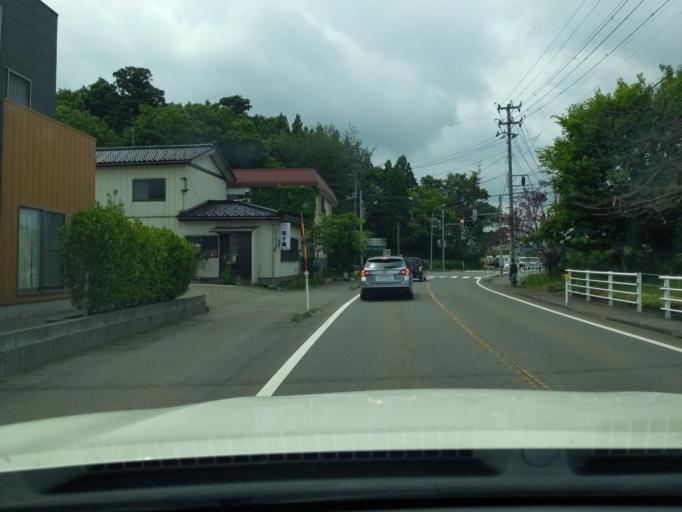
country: JP
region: Niigata
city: Kashiwazaki
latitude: 37.3501
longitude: 138.5702
